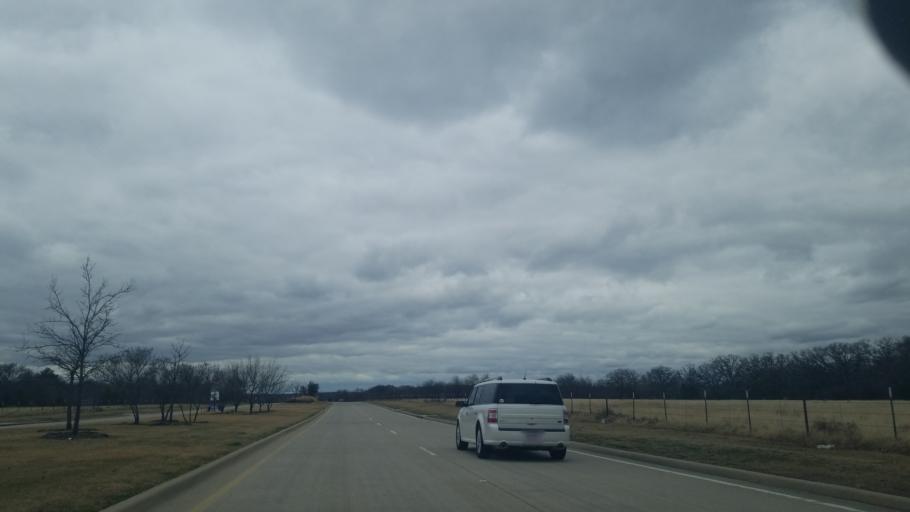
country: US
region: Texas
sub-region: Denton County
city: Copper Canyon
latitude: 33.1127
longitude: -97.0788
